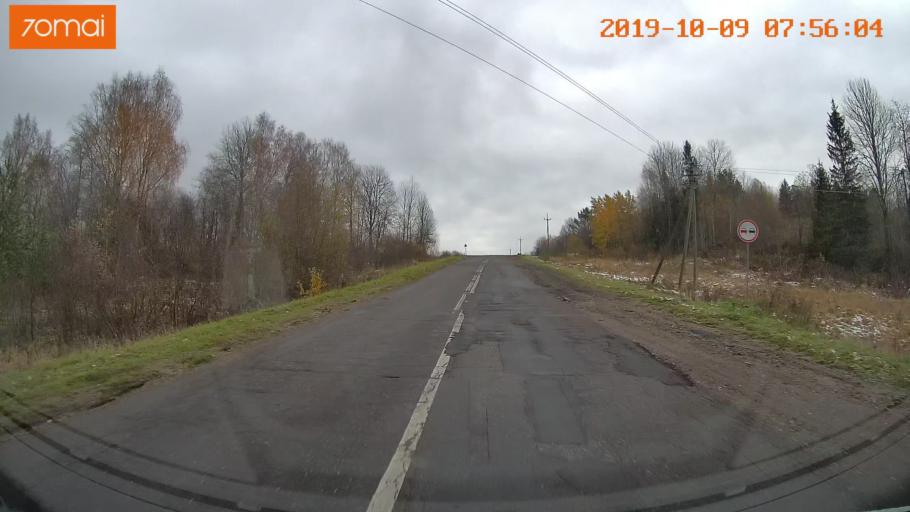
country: RU
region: Jaroslavl
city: Kukoboy
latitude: 58.6988
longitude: 39.9307
